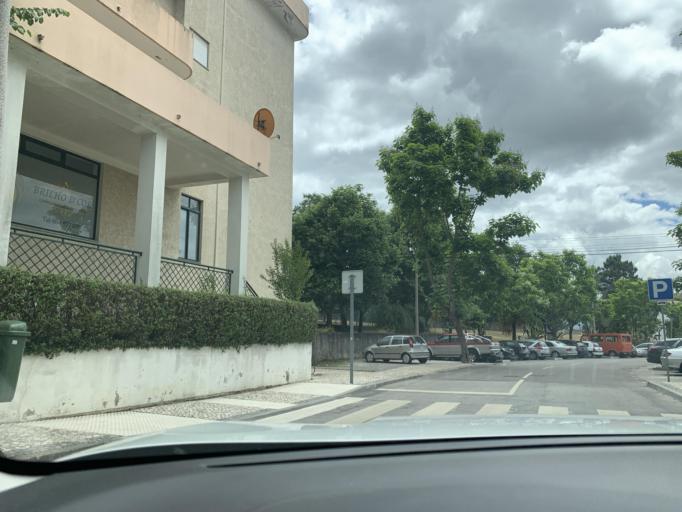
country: PT
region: Viseu
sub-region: Viseu
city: Rio de Loba
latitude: 40.6500
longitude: -7.8906
